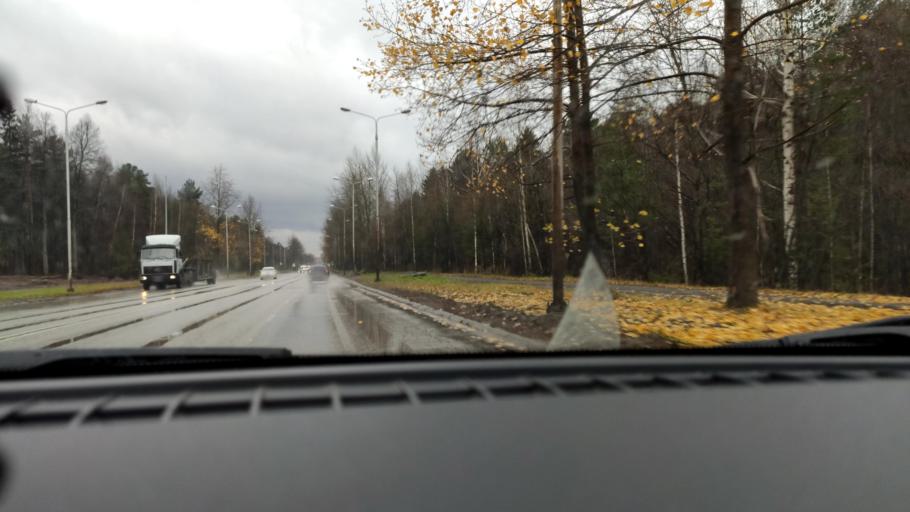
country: RU
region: Perm
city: Perm
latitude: 58.0890
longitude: 56.3809
